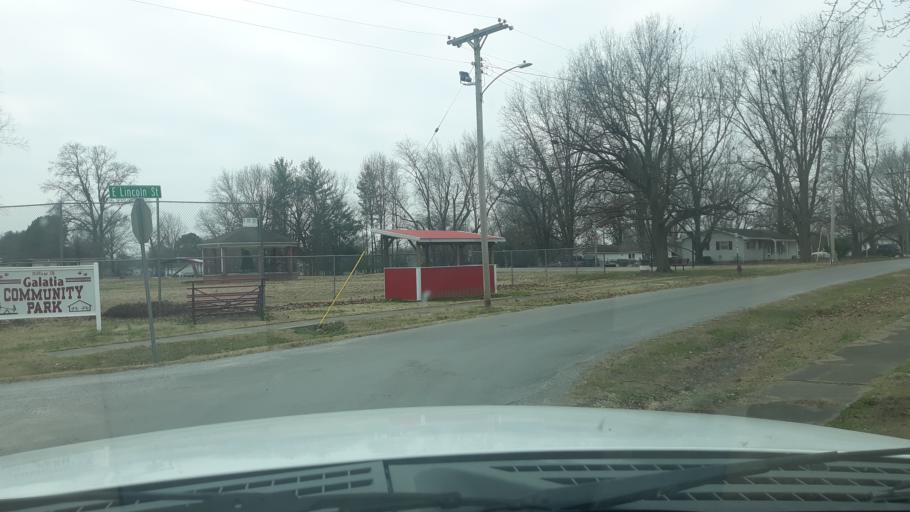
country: US
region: Illinois
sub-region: Saline County
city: Harrisburg
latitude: 37.8389
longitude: -88.6094
